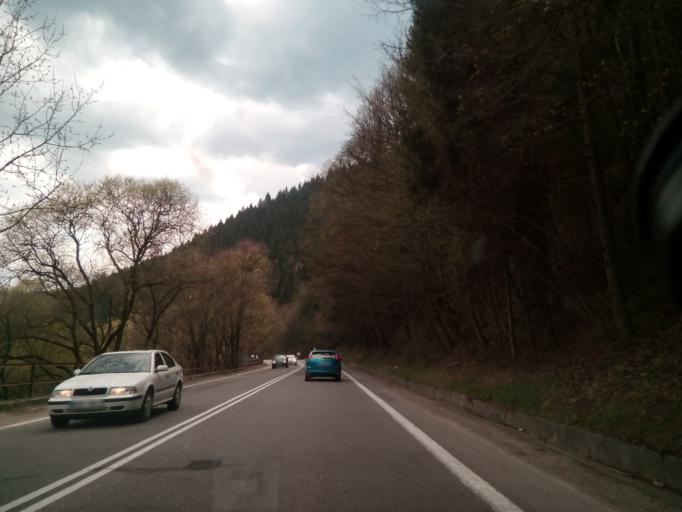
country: SK
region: Zilinsky
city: Ruzomberok
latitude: 49.1132
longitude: 19.2244
